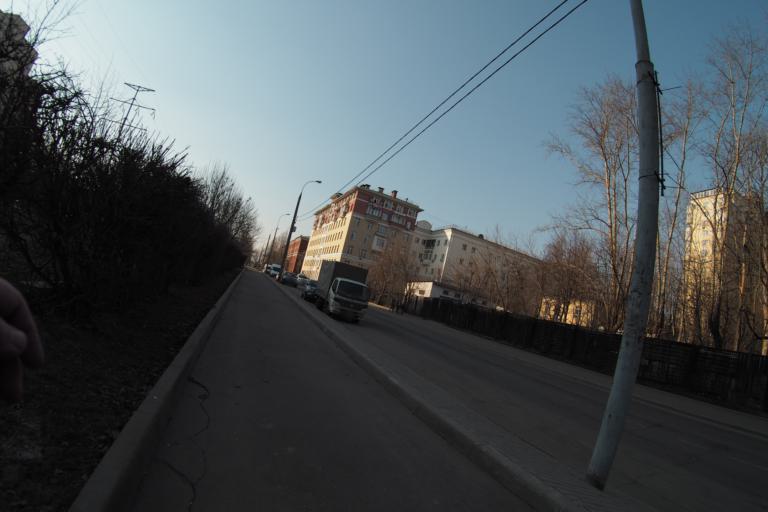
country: RU
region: Moskovskaya
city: Bol'shaya Setun'
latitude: 55.7171
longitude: 37.3974
